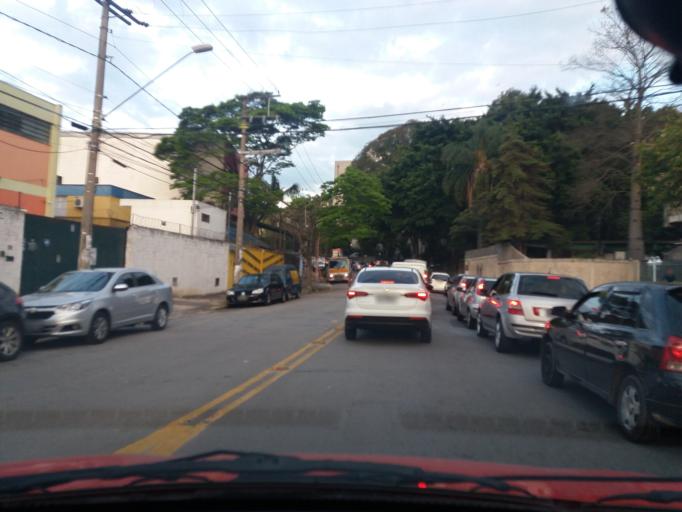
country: BR
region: Sao Paulo
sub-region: Taboao Da Serra
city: Taboao da Serra
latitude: -23.6044
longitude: -46.7488
